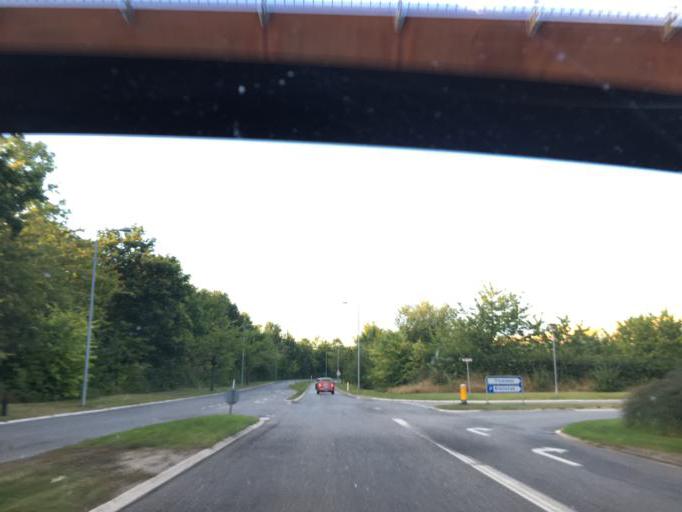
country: DK
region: Capital Region
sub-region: Horsholm Kommune
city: Horsholm
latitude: 55.8799
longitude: 12.4940
